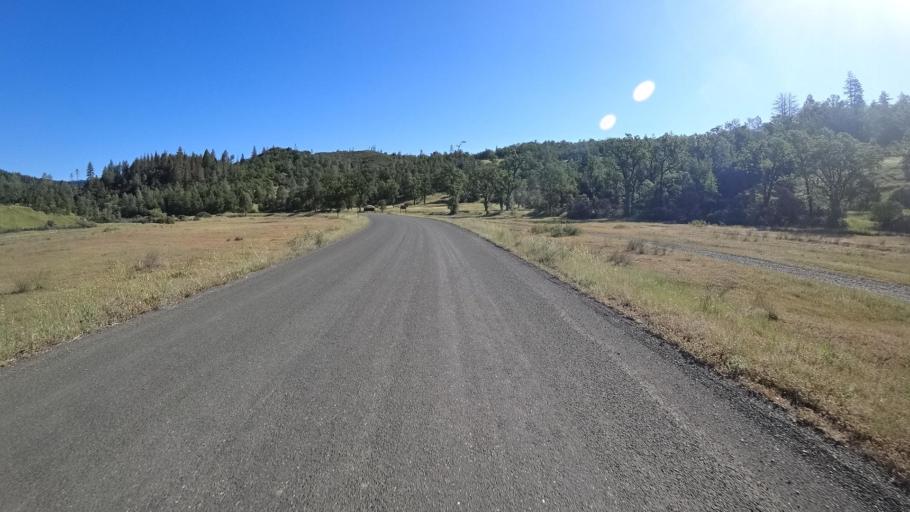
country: US
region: California
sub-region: Lake County
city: Upper Lake
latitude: 39.4126
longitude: -122.9749
